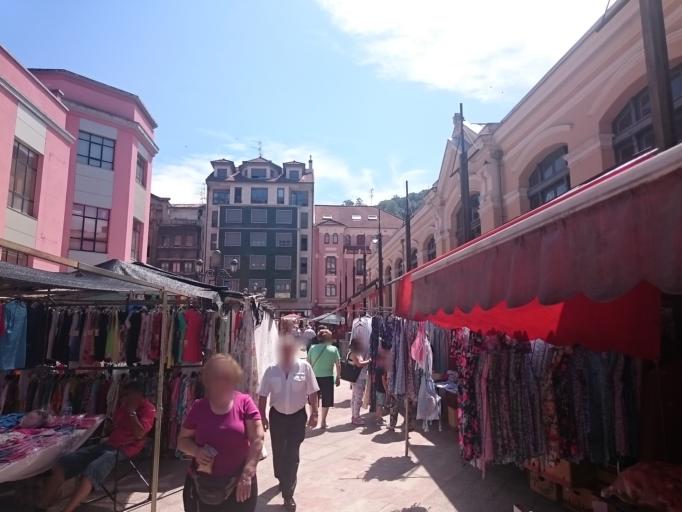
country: ES
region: Asturias
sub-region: Province of Asturias
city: Mieres
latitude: 43.2517
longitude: -5.7745
